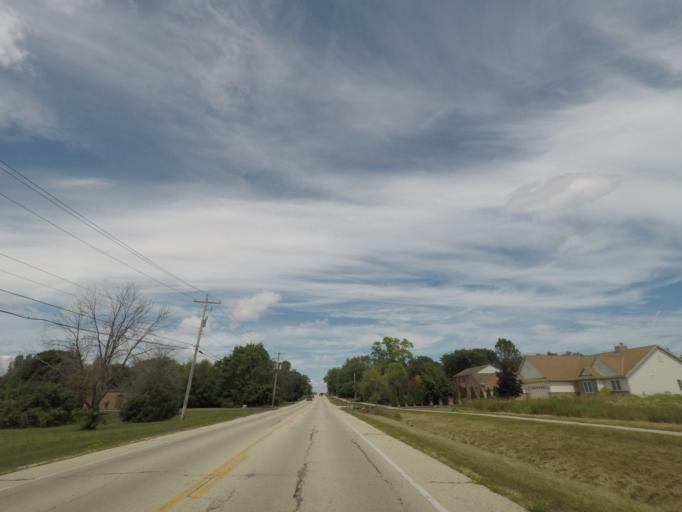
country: US
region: Wisconsin
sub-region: Milwaukee County
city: Greendale
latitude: 42.9098
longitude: -87.9797
